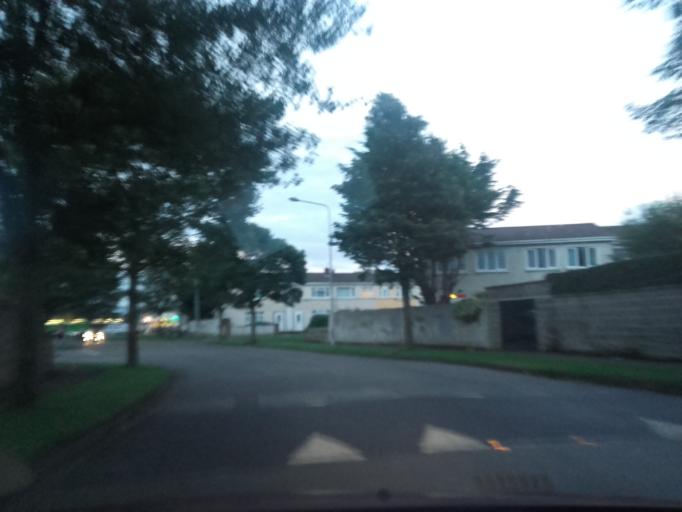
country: IE
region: Leinster
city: Tallaght
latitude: 53.2868
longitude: -6.3844
